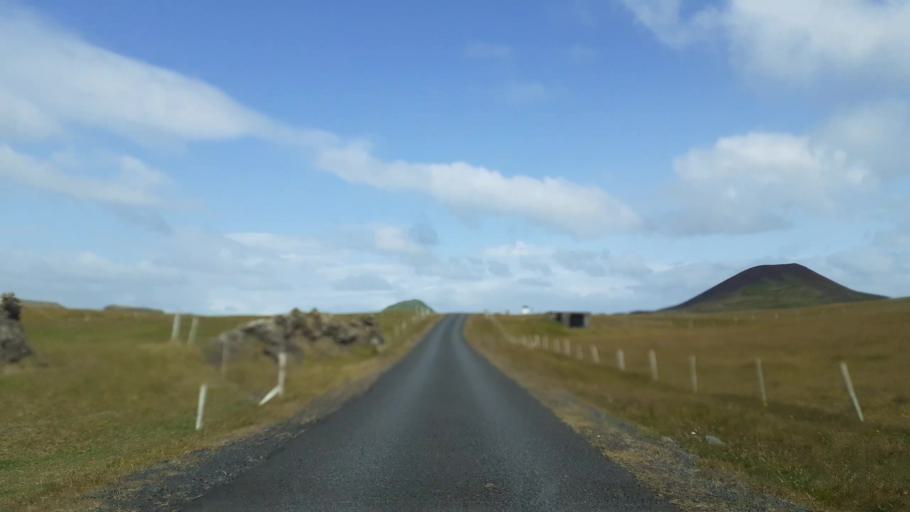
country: IS
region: South
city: Vestmannaeyjar
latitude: 63.4194
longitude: -20.2806
